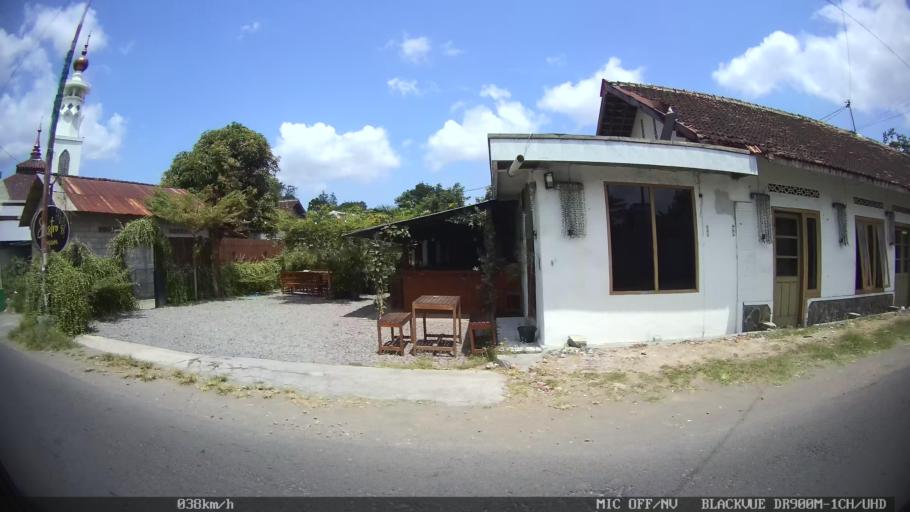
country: ID
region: Daerah Istimewa Yogyakarta
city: Sewon
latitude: -7.8699
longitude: 110.3528
